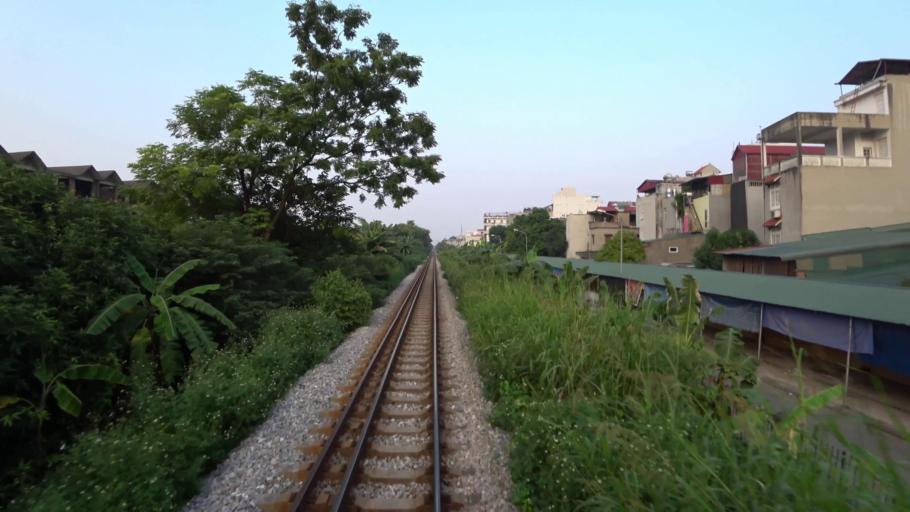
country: VN
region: Ha Noi
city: Trau Quy
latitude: 21.0786
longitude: 105.9095
